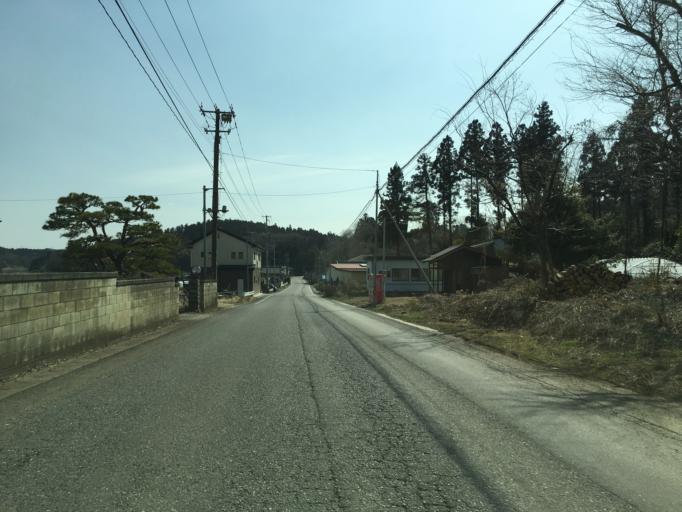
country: JP
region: Fukushima
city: Ishikawa
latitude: 37.1455
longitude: 140.3986
